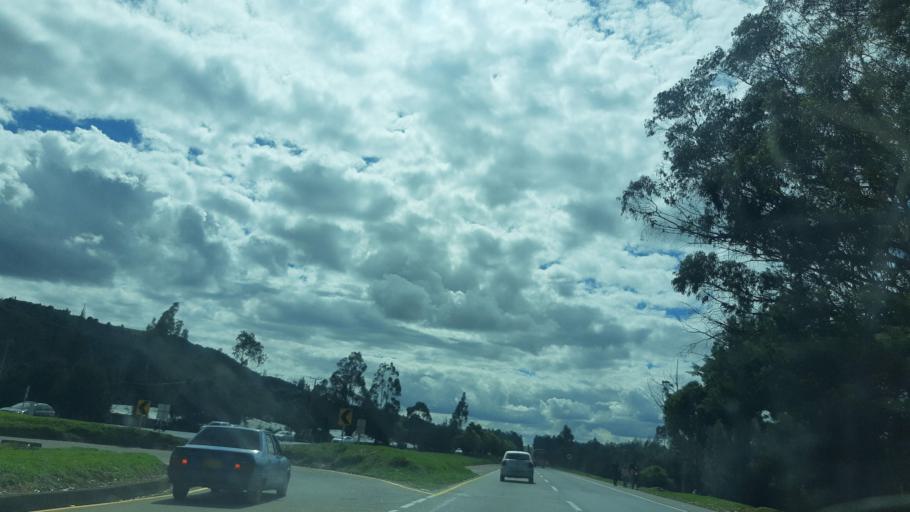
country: CO
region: Cundinamarca
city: Sesquile
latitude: 5.0493
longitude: -73.8171
